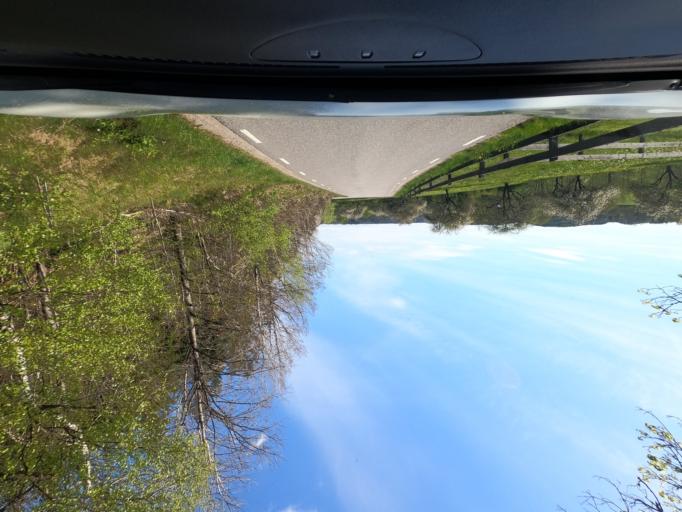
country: SE
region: Vaestra Goetaland
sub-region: Harryda Kommun
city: Ravlanda
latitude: 57.6364
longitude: 12.4977
